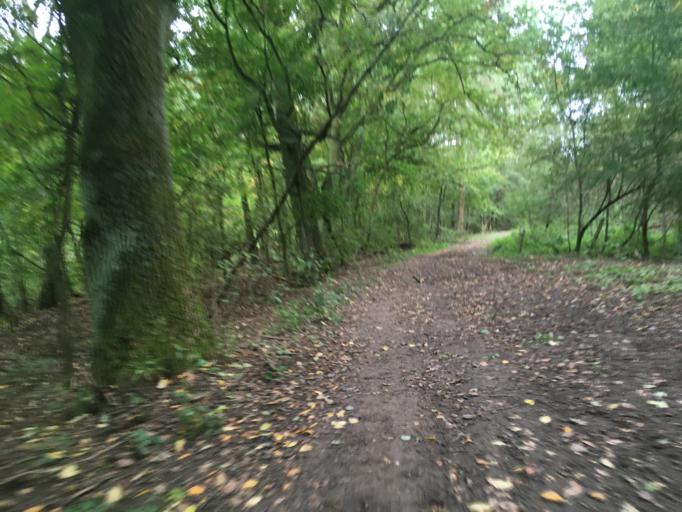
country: DE
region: Brandenburg
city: Falkensee
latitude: 52.5185
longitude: 13.0981
